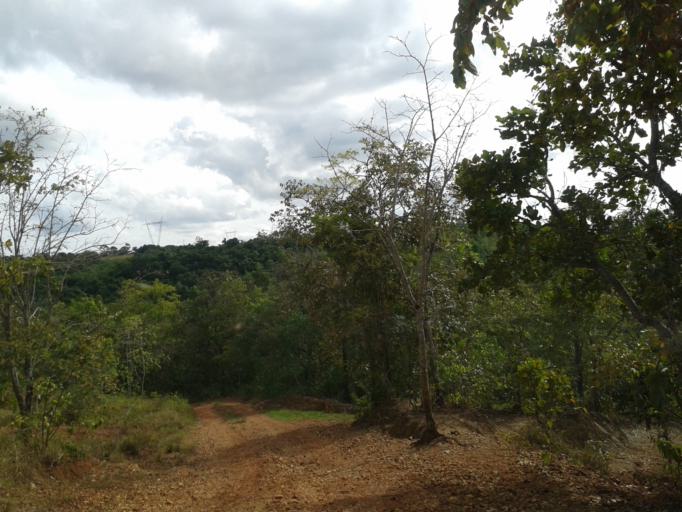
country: BR
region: Minas Gerais
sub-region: Campina Verde
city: Campina Verde
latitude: -19.4347
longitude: -49.6187
